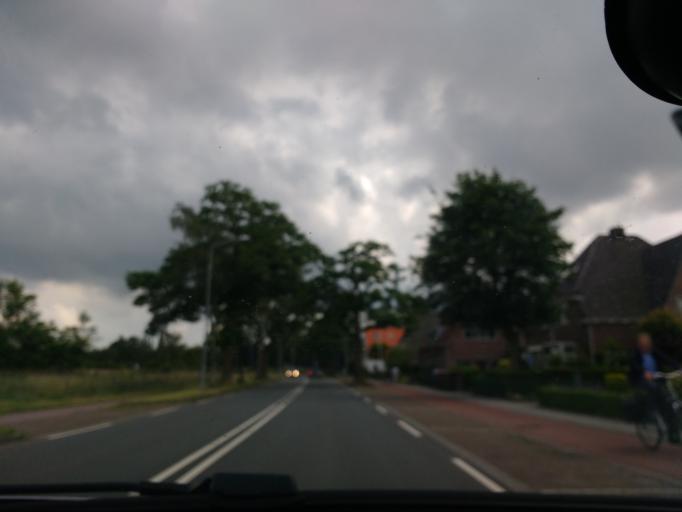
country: NL
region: Gelderland
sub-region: Gemeente Wageningen
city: Wageningen
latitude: 51.9763
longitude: 5.6808
